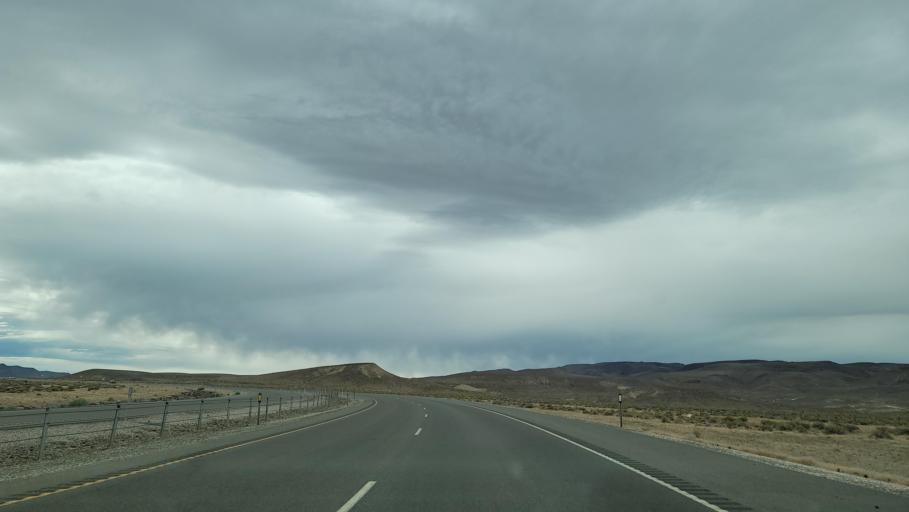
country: US
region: Nevada
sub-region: Lyon County
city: Silver Springs
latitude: 39.4065
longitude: -119.2701
